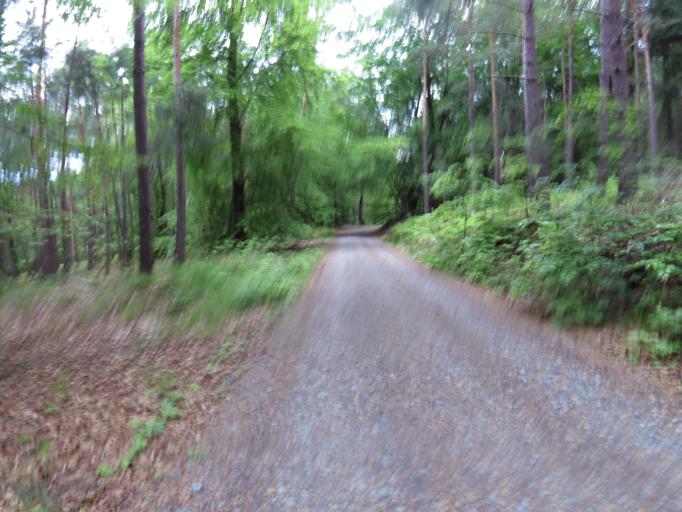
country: DE
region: Rheinland-Pfalz
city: Neidenfels
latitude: 49.4178
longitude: 8.0742
